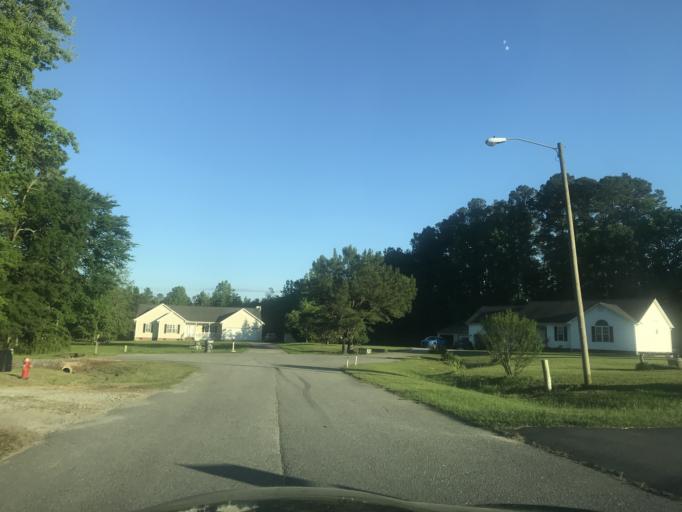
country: US
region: North Carolina
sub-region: Johnston County
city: Archer Lodge
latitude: 35.6807
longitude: -78.3402
